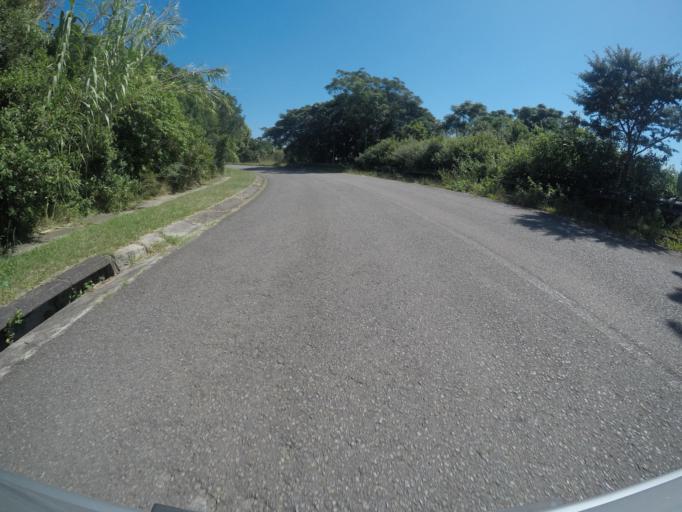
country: ZA
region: Eastern Cape
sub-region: Buffalo City Metropolitan Municipality
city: East London
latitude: -32.9713
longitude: 27.9210
